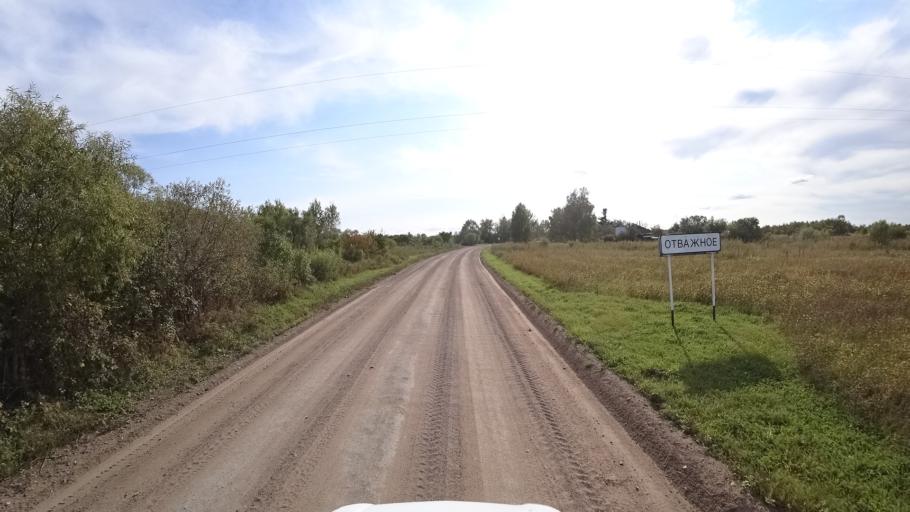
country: RU
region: Amur
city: Arkhara
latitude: 49.3680
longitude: 130.1316
